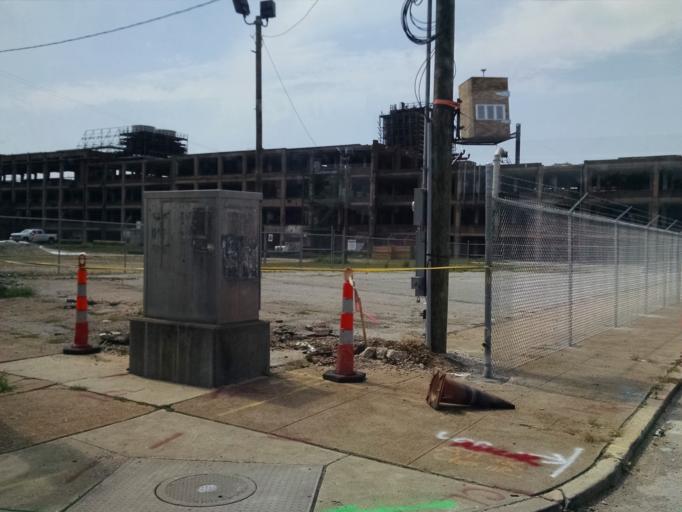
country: US
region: Missouri
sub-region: City of Saint Louis
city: St. Louis
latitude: 38.6568
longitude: -90.2200
